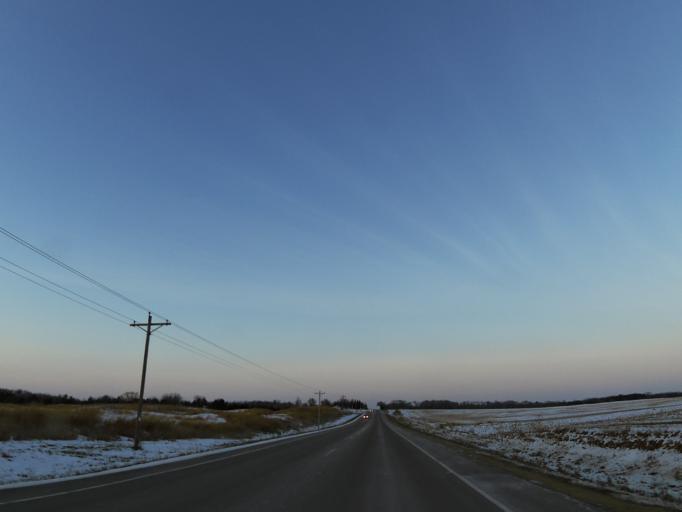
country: US
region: Minnesota
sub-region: Washington County
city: Lake Saint Croix Beach
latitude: 44.9023
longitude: -92.7311
